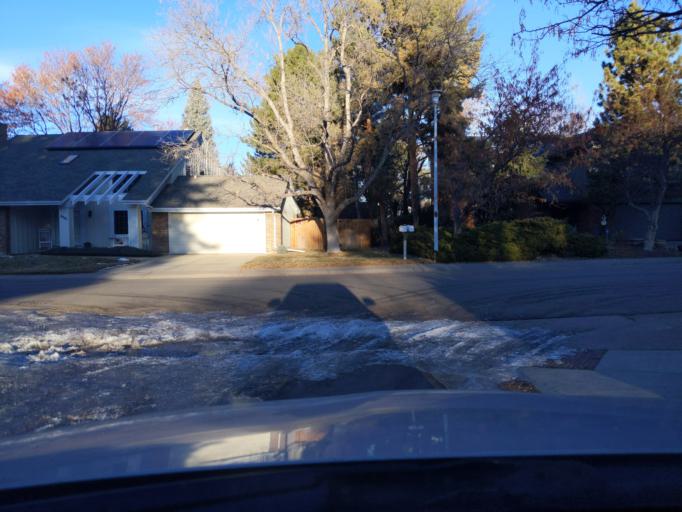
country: US
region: Colorado
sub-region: Arapahoe County
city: Centennial
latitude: 39.5741
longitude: -104.8907
